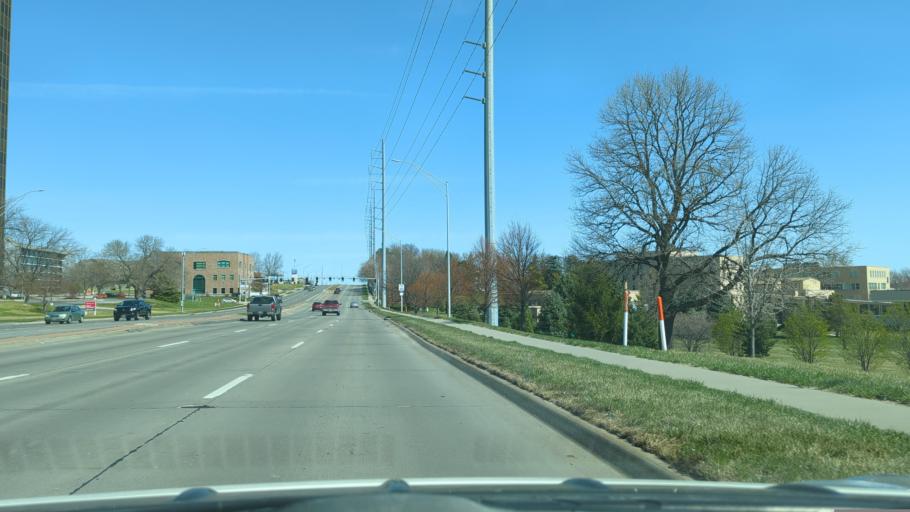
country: US
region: Nebraska
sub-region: Douglas County
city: Ralston
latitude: 41.2382
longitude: -96.0238
